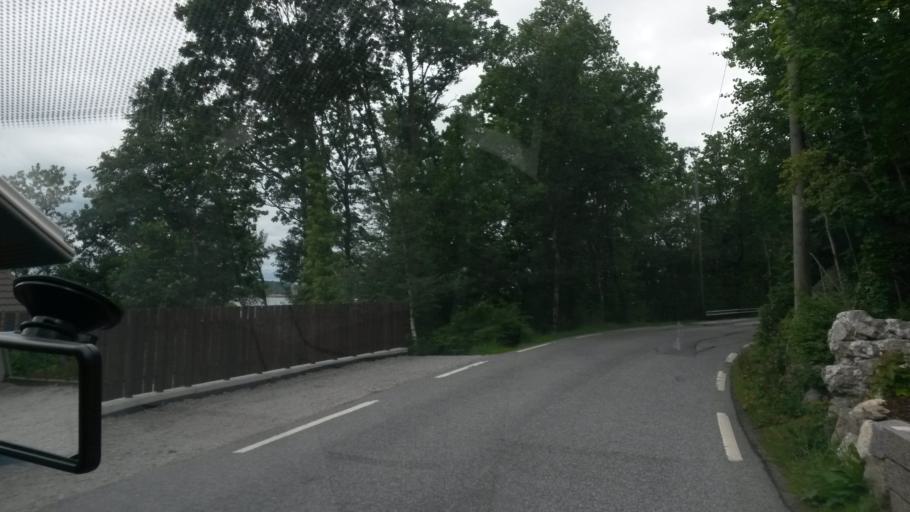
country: NO
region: Rogaland
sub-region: Sandnes
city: Sandnes
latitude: 58.8830
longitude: 5.7754
